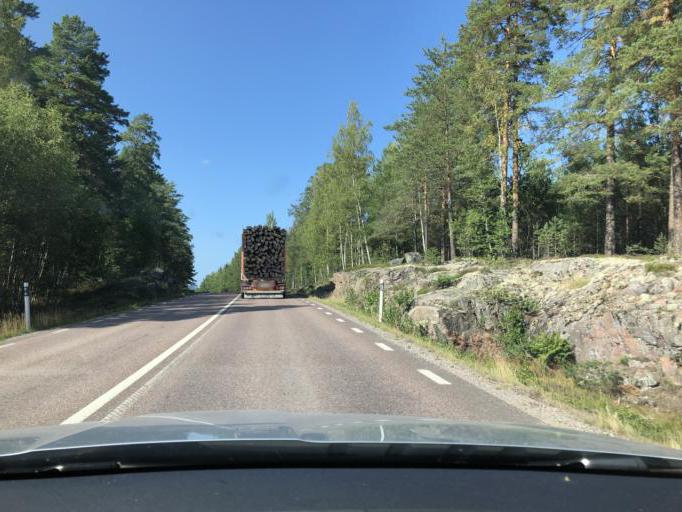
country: SE
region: Dalarna
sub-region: Faluns Kommun
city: Falun
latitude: 60.5651
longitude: 15.7778
